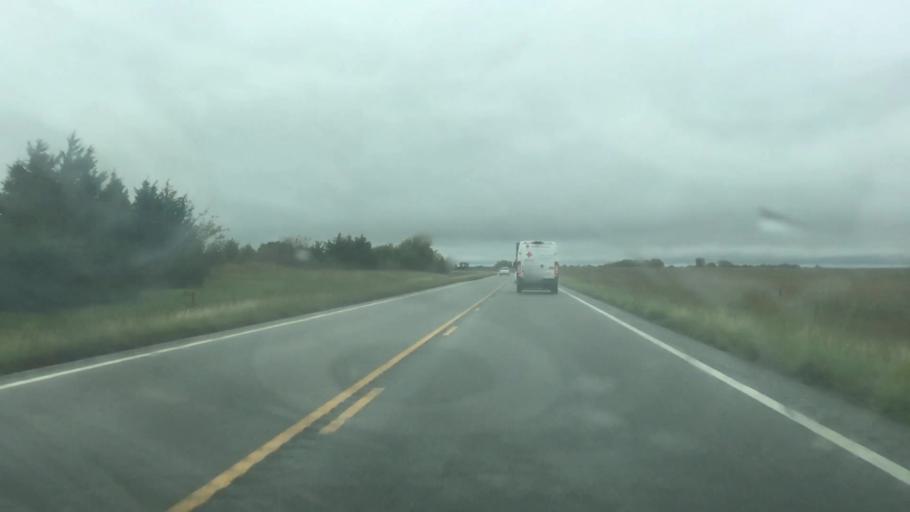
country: US
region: Kansas
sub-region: Anderson County
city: Garnett
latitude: 38.1468
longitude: -95.3237
